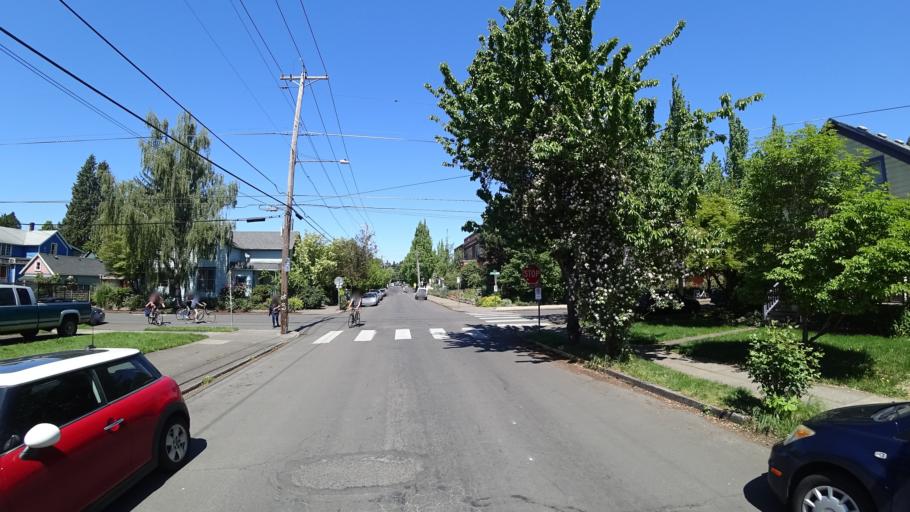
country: US
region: Oregon
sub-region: Multnomah County
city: Portland
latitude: 45.5141
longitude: -122.6296
